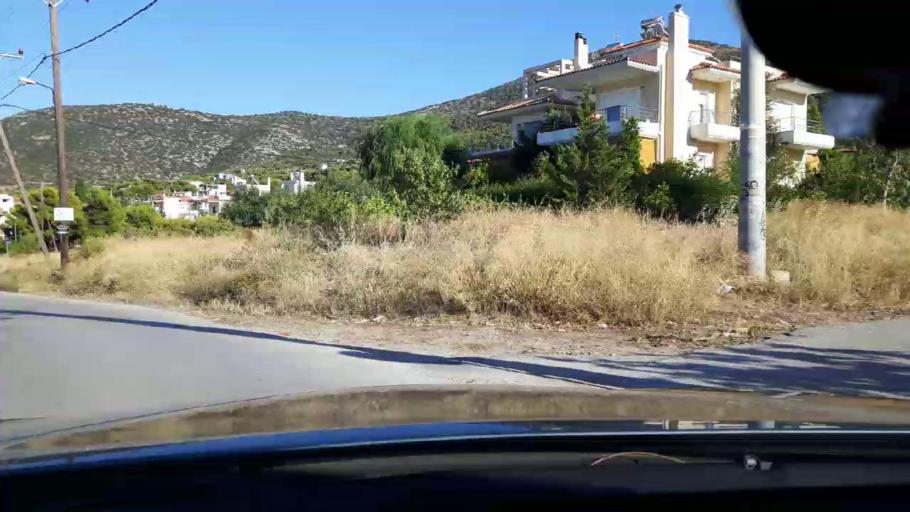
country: GR
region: Attica
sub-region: Nomarchia Anatolikis Attikis
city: Limin Mesoyaias
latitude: 37.8608
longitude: 24.0384
